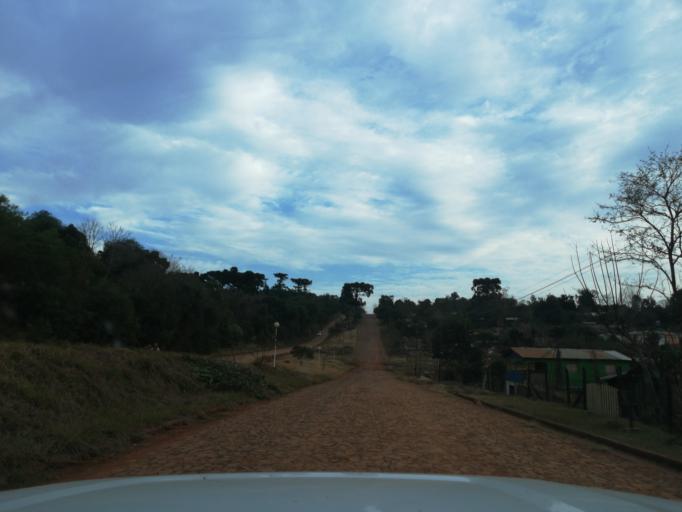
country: AR
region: Misiones
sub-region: Departamento de San Pedro
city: San Pedro
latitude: -26.6288
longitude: -54.0936
